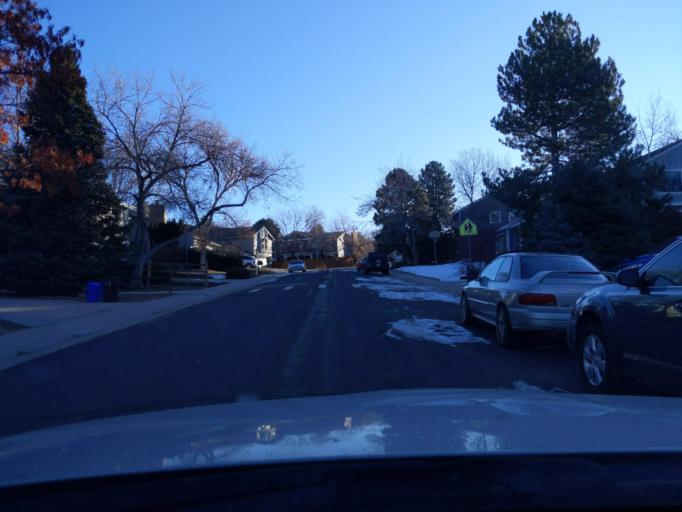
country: US
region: Colorado
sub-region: Arapahoe County
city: Centennial
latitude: 39.5729
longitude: -104.8892
